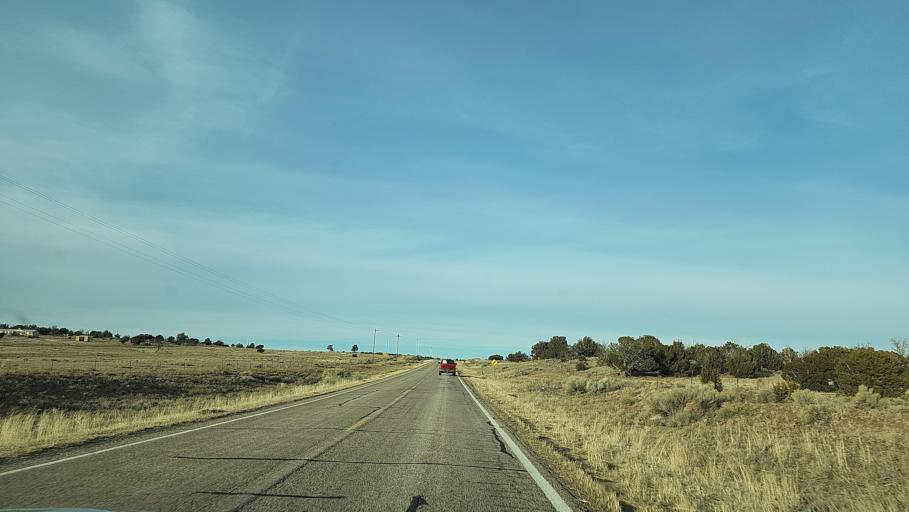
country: US
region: New Mexico
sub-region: Catron County
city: Reserve
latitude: 34.3799
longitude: -108.4585
